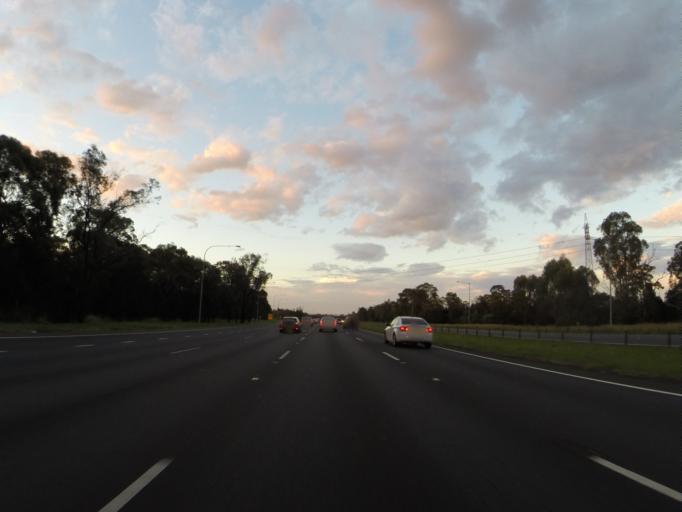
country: AU
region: New South Wales
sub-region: Campbelltown Municipality
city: Glenfield
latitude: -33.9620
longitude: 150.8755
